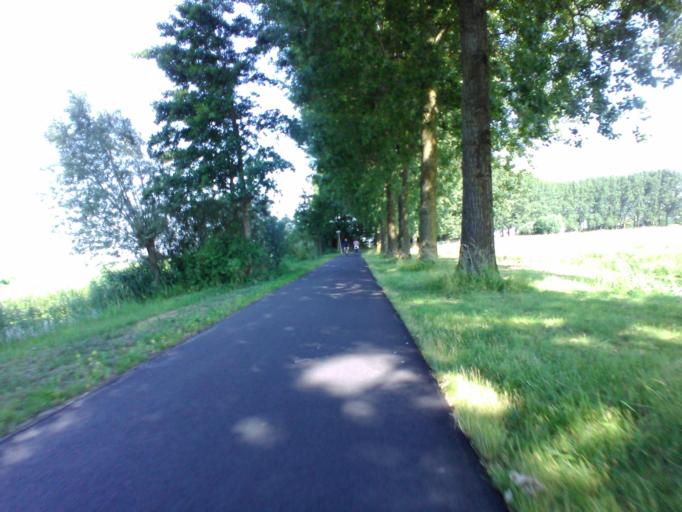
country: NL
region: South Holland
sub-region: Gemeente Alphen aan den Rijn
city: Alphen aan den Rijn
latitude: 52.1586
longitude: 4.6963
